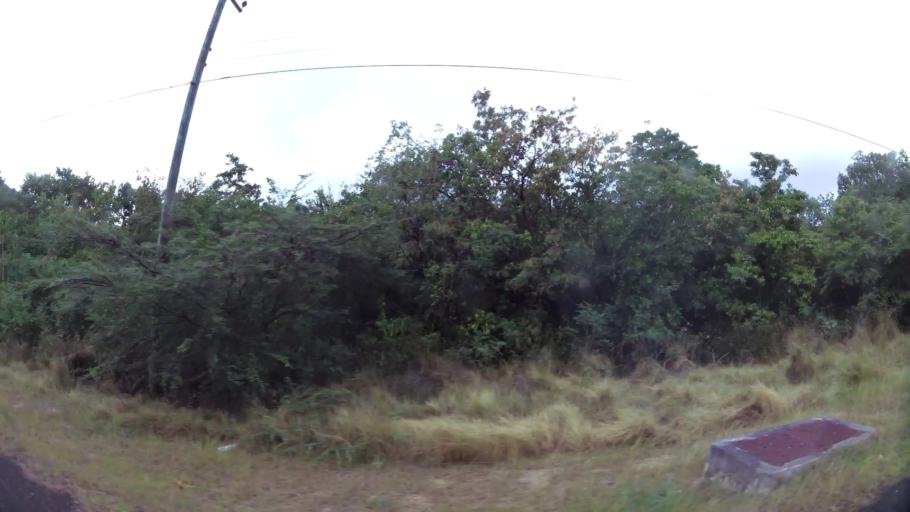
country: KN
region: Saint James Windwa
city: Newcastle
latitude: 17.2028
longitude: -62.6051
